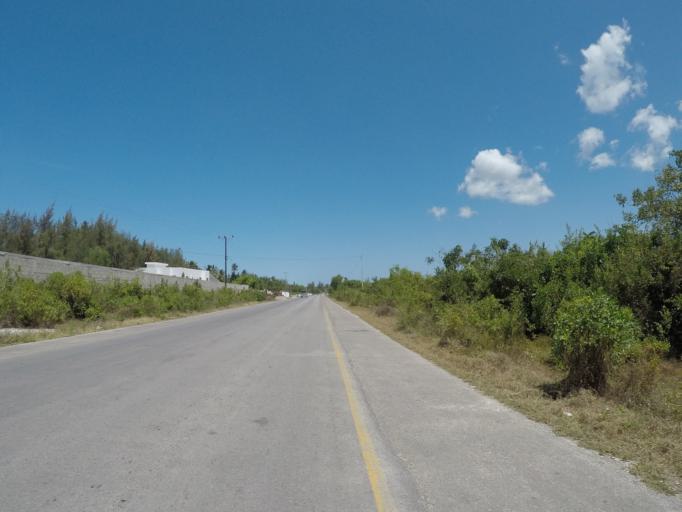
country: TZ
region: Zanzibar Central/South
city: Nganane
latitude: -6.2786
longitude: 39.5346
